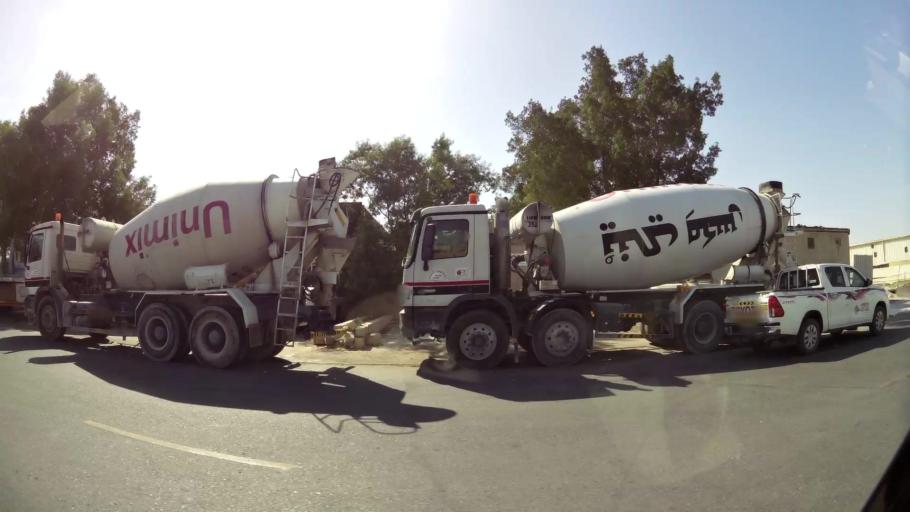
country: AE
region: Dubai
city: Dubai
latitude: 25.1188
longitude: 55.2212
